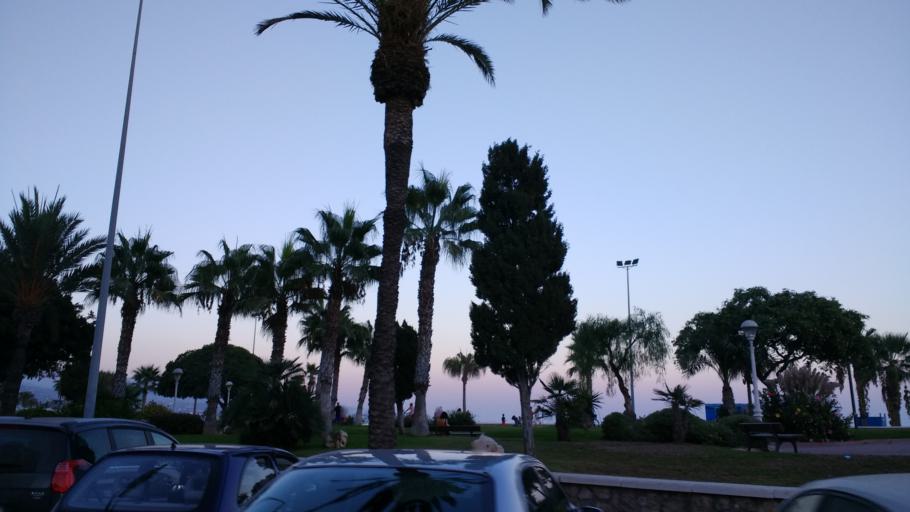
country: ES
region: Andalusia
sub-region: Provincia de Malaga
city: Velez-Malaga
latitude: 36.7420
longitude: -4.0895
